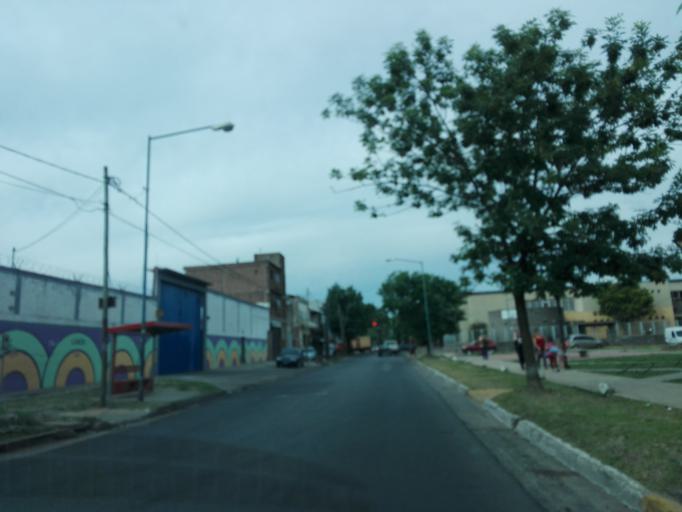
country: AR
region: Buenos Aires
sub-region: Partido de Lanus
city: Lanus
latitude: -34.7023
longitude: -58.3656
